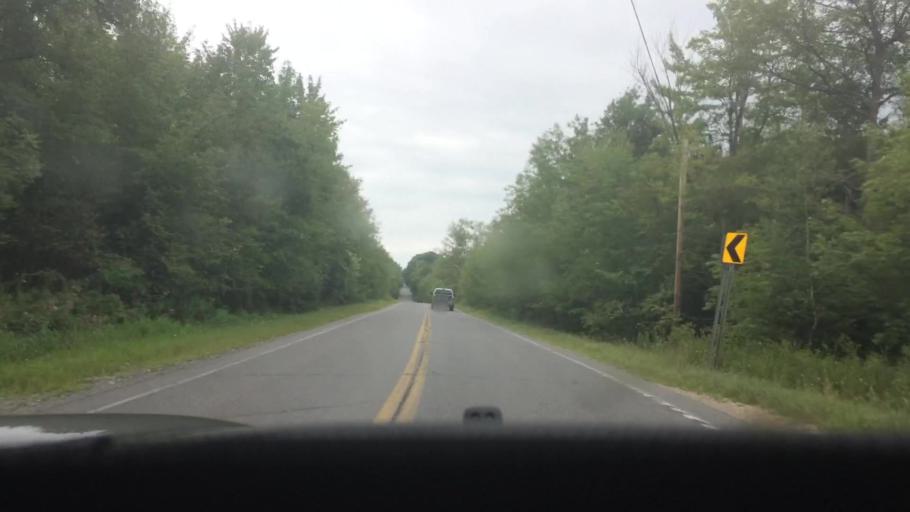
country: US
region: New York
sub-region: St. Lawrence County
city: Canton
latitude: 44.5005
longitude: -75.2160
